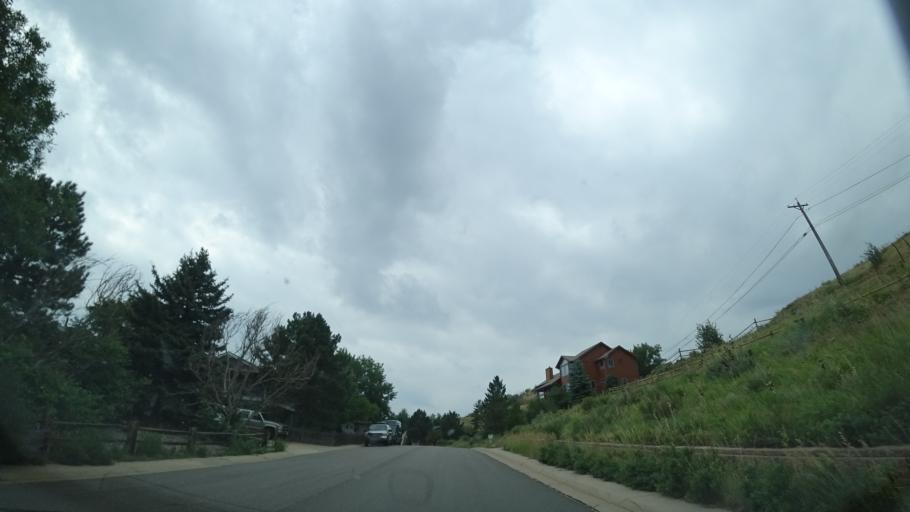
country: US
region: Colorado
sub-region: Jefferson County
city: West Pleasant View
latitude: 39.6941
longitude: -105.1516
